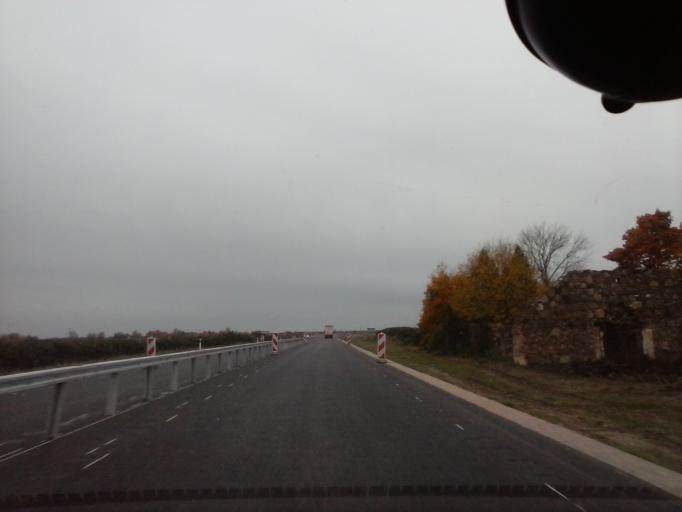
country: EE
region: Jogevamaa
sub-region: Poltsamaa linn
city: Poltsamaa
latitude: 58.6423
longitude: 26.0646
